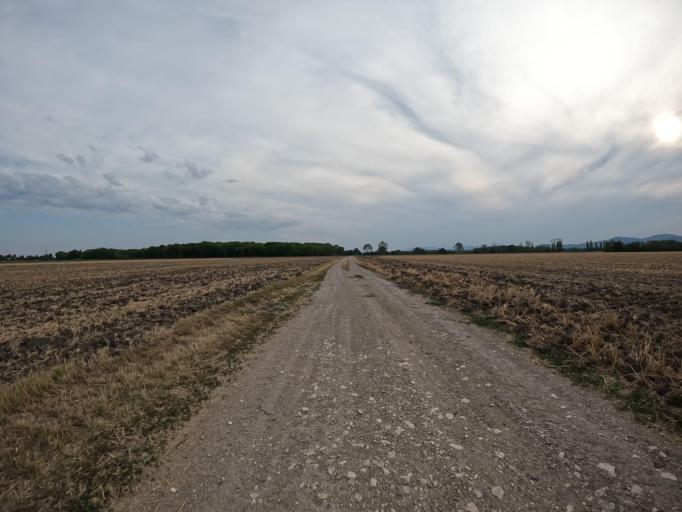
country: AT
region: Lower Austria
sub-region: Politischer Bezirk Baden
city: Trumau
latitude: 48.0012
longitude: 16.3287
